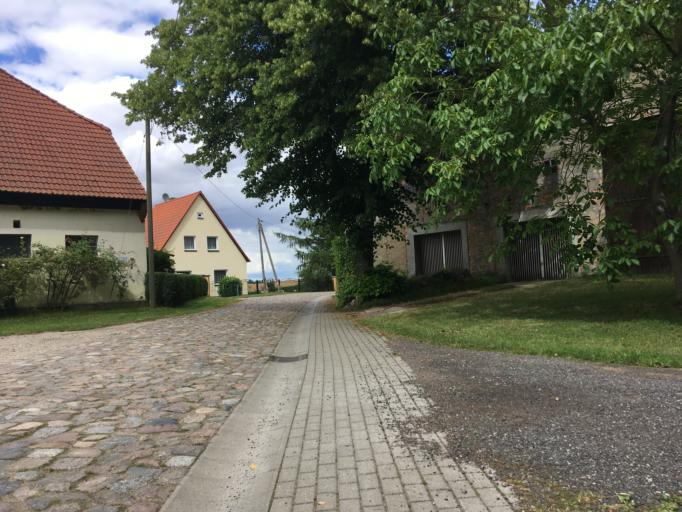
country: DE
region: Brandenburg
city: Gramzow
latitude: 53.2565
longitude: 14.0113
